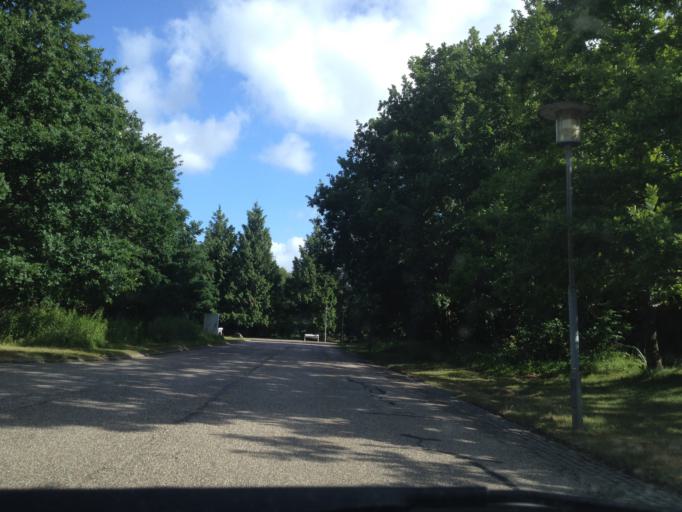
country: DK
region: Capital Region
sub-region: Horsholm Kommune
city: Horsholm
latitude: 55.8725
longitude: 12.4925
